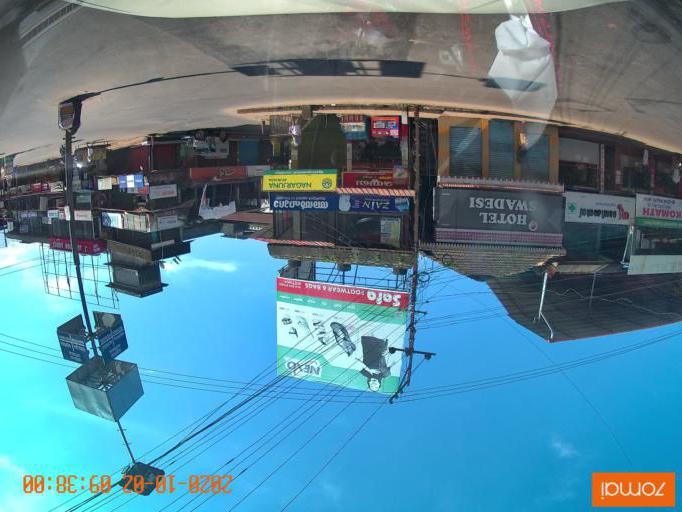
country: IN
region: Kerala
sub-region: Kozhikode
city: Nadapuram
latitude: 11.6541
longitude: 75.7537
